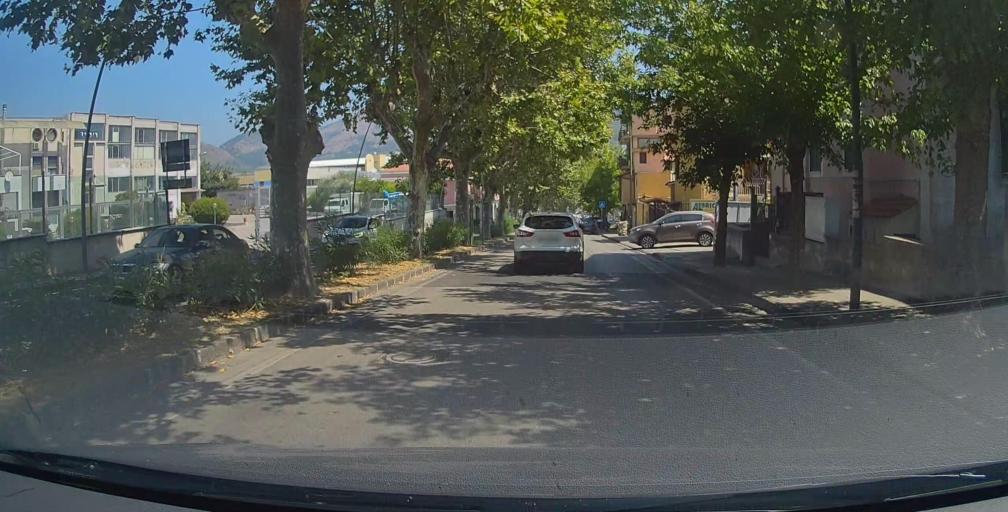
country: IT
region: Campania
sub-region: Provincia di Salerno
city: Cava De Tirreni
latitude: 40.7117
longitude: 14.7009
